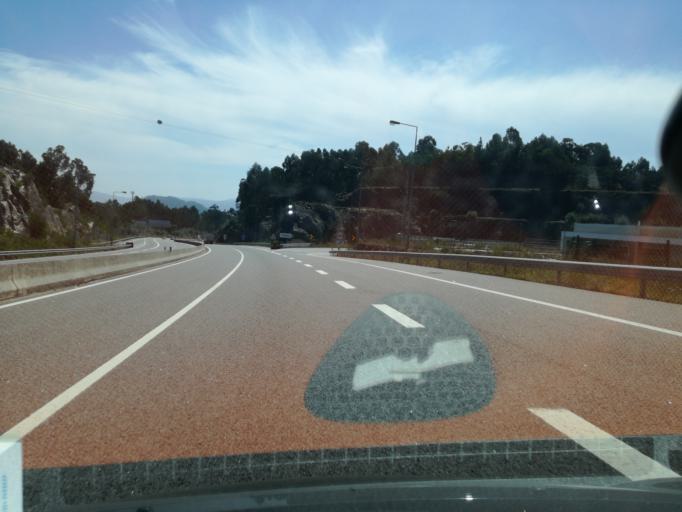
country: PT
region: Viana do Castelo
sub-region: Viana do Castelo
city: Meadela
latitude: 41.7430
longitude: -8.7970
